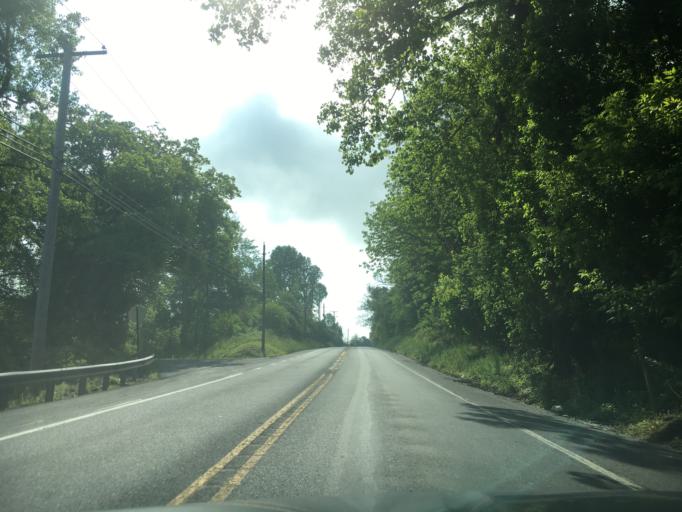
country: US
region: Pennsylvania
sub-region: Berks County
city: New Berlinville
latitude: 40.3659
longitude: -75.7033
